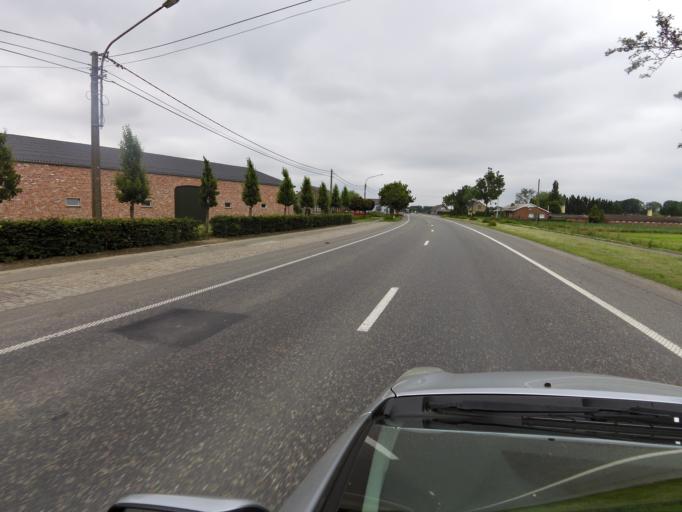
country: BE
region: Flanders
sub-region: Provincie West-Vlaanderen
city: Ieper
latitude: 50.8861
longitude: 2.8664
